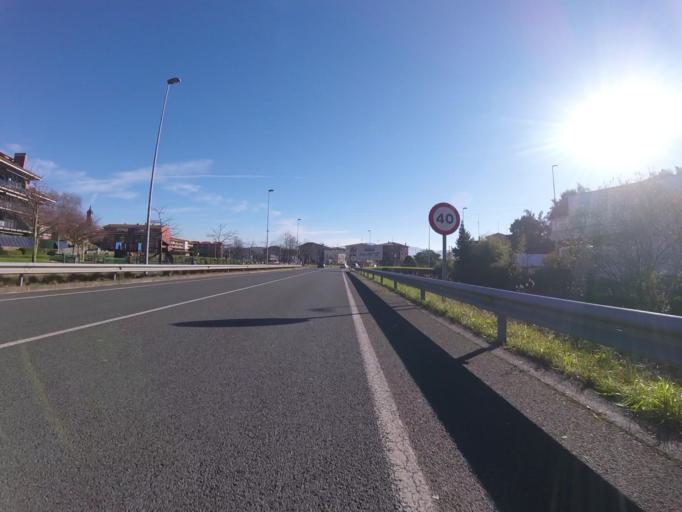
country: ES
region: Basque Country
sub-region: Provincia de Guipuzcoa
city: Fuenterrabia
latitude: 43.3616
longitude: -1.7962
